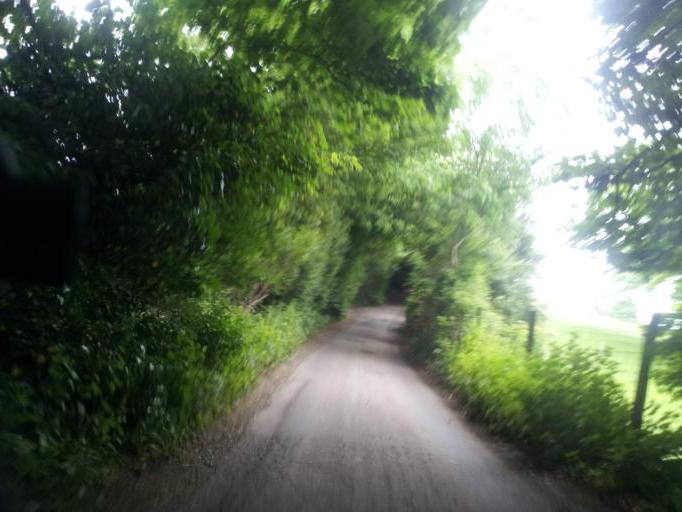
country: GB
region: England
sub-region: Kent
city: Boxley
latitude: 51.3054
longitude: 0.5468
